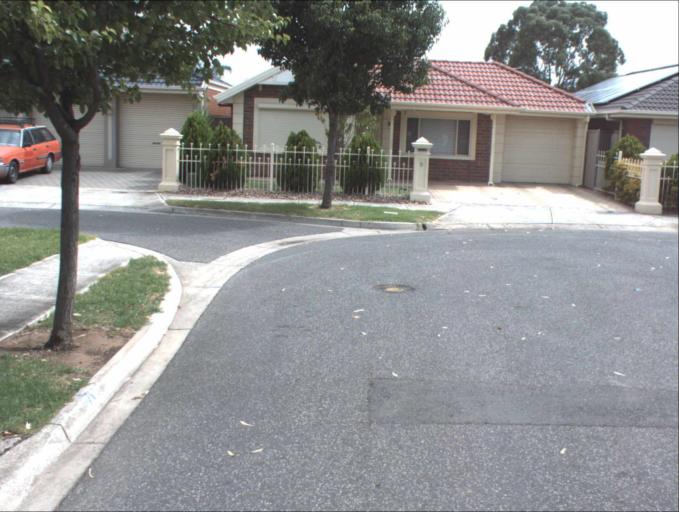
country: AU
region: South Australia
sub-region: Charles Sturt
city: Woodville
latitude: -34.8689
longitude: 138.5610
